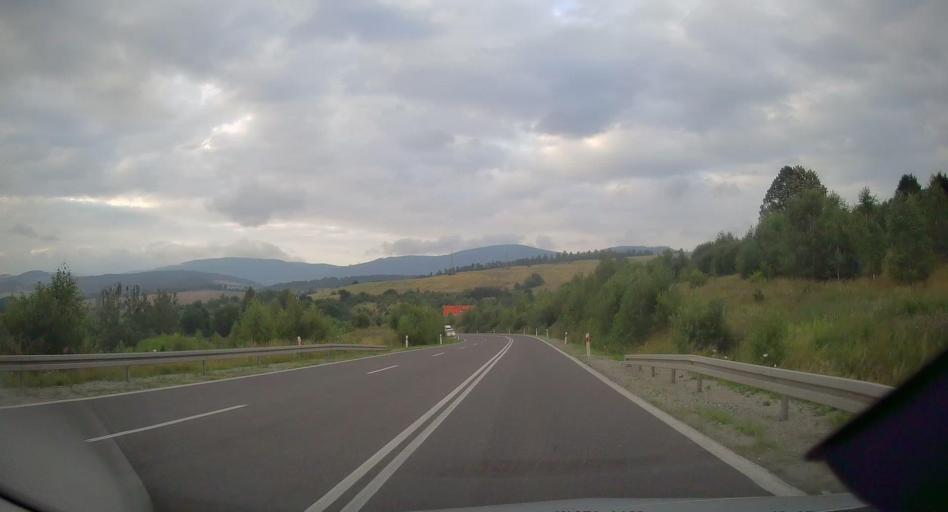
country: PL
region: Lower Silesian Voivodeship
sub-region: Powiat klodzki
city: Nowa Ruda
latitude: 50.5891
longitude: 16.5239
